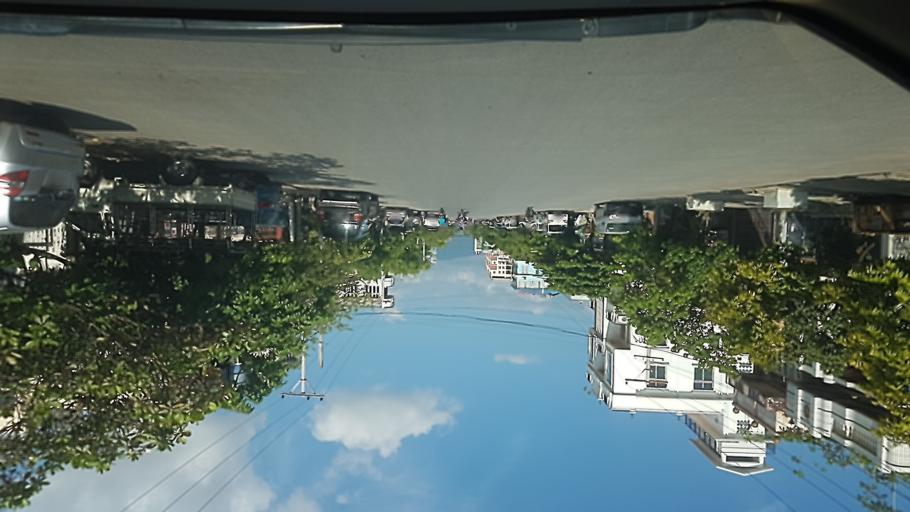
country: MM
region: Mandalay
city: Mandalay
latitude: 21.9814
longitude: 96.0894
